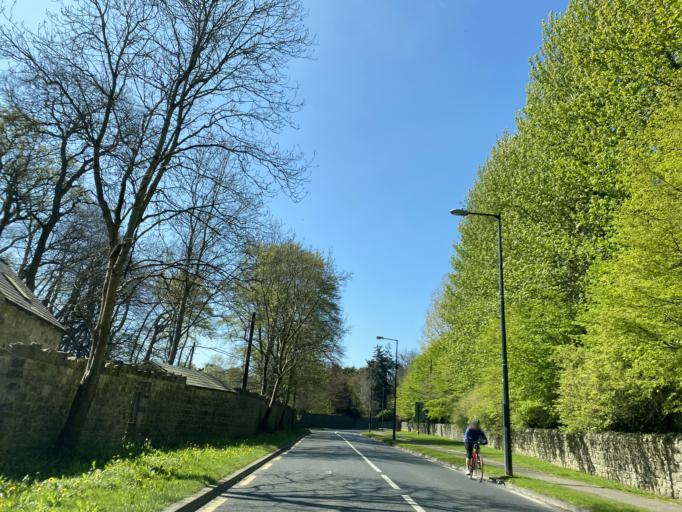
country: IE
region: Leinster
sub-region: Kildare
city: Kill
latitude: 53.3081
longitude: -6.6117
